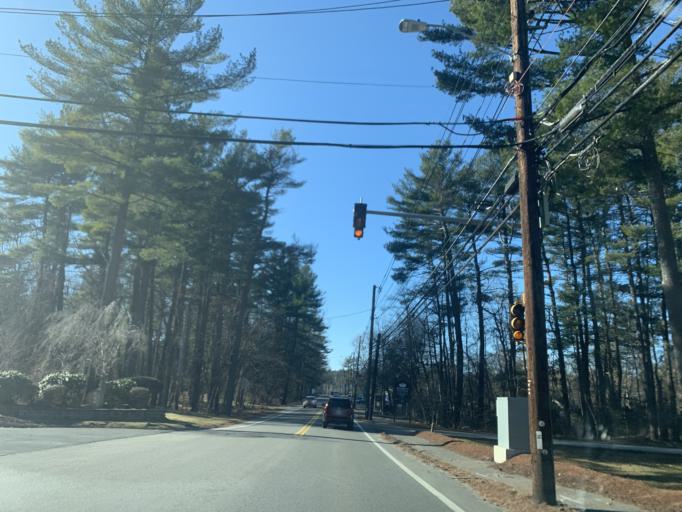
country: US
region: Massachusetts
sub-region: Middlesex County
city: Sudbury
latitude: 42.3606
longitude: -71.4422
